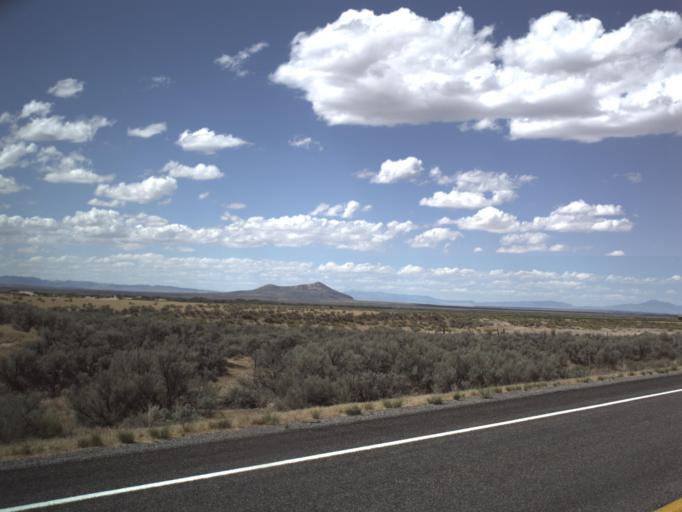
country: US
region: Utah
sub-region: Millard County
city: Fillmore
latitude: 39.1339
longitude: -112.3621
